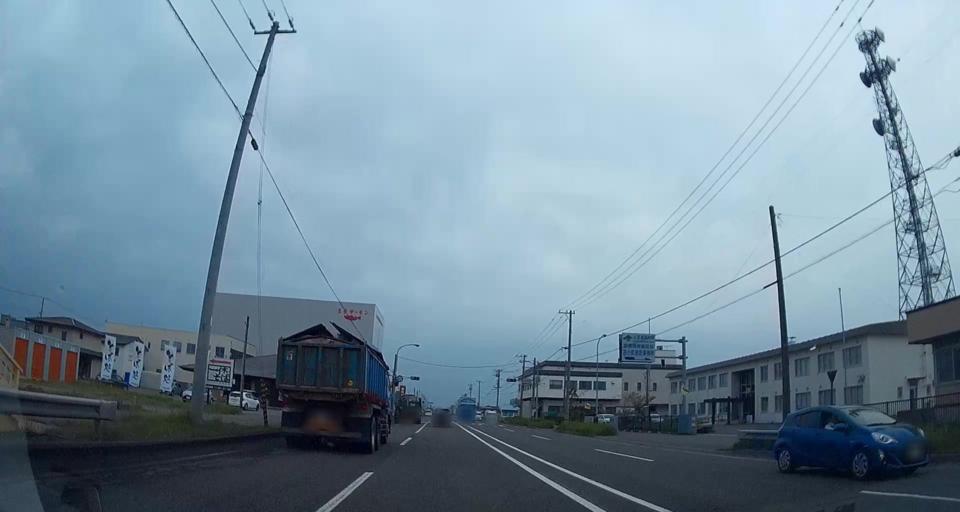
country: JP
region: Hokkaido
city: Tomakomai
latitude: 42.6193
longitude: 141.5541
